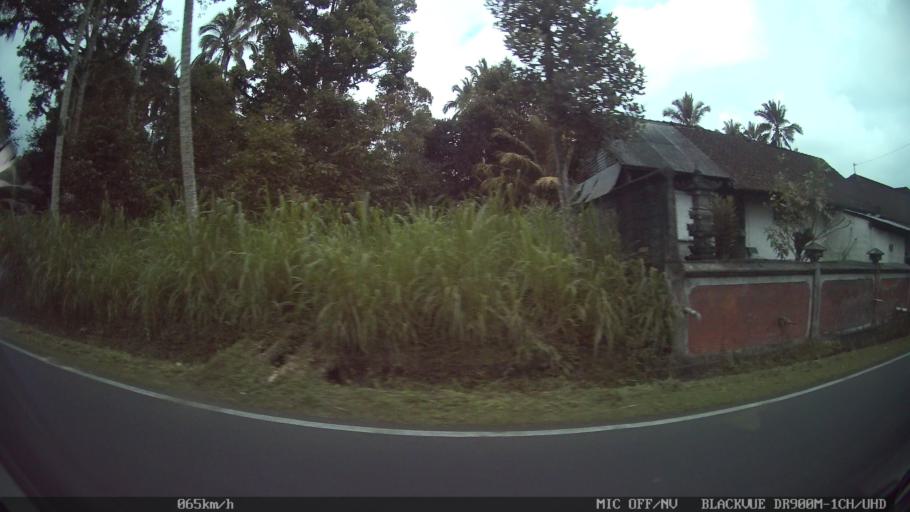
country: ID
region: Bali
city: Banjar Kubu
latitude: -8.3934
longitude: 115.4199
